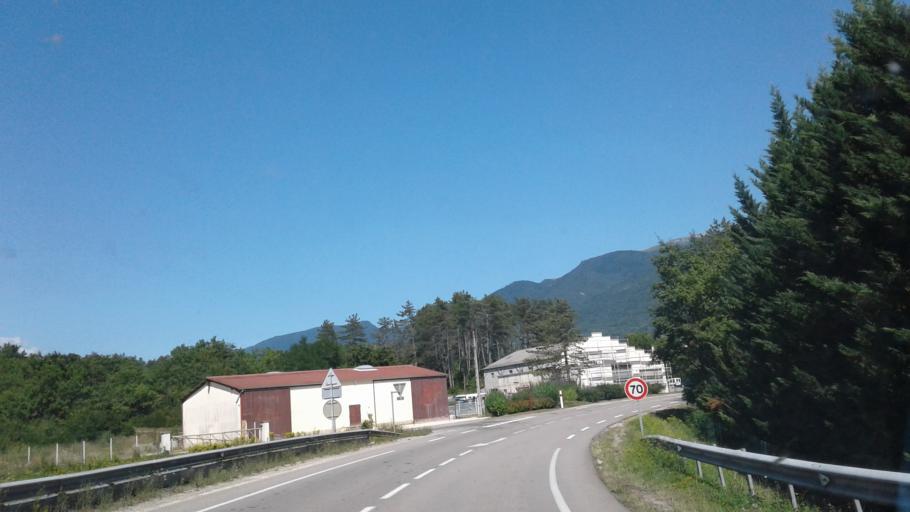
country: FR
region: Rhone-Alpes
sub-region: Departement de l'Ain
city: Artemare
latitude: 45.8628
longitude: 5.6813
